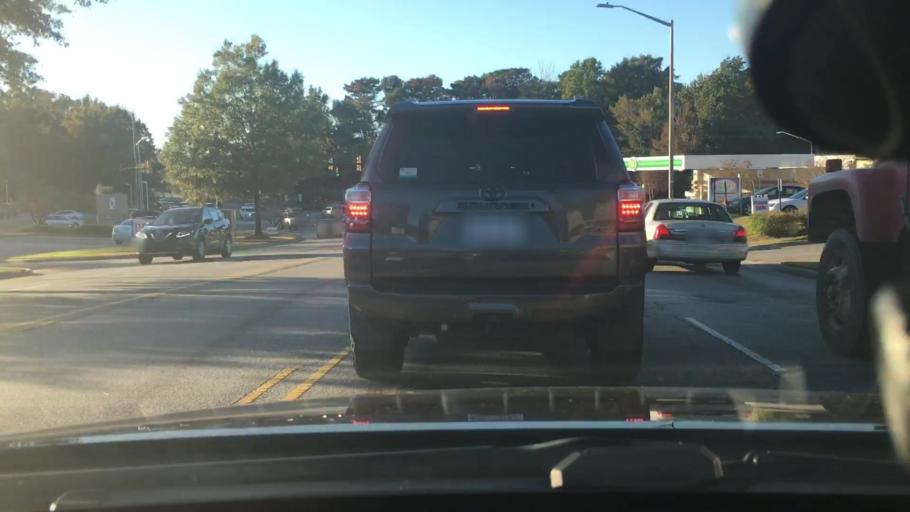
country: US
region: North Carolina
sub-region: Pitt County
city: Greenville
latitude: 35.5905
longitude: -77.3773
